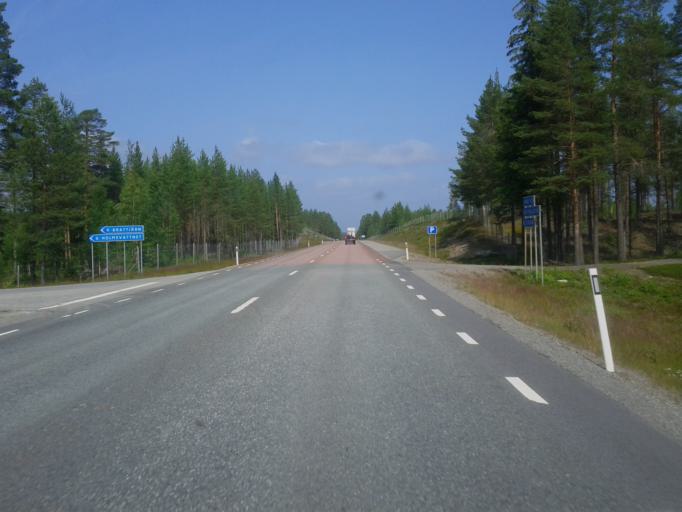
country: SE
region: Vaesterbotten
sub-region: Skelleftea Kommun
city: Burea
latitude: 64.5917
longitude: 21.2128
